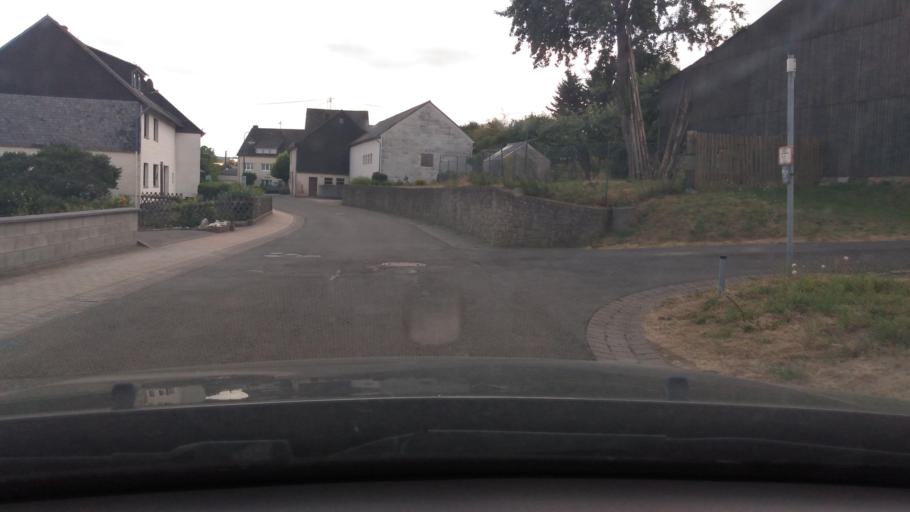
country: DE
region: Rheinland-Pfalz
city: Kommen
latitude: 49.8799
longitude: 7.1273
